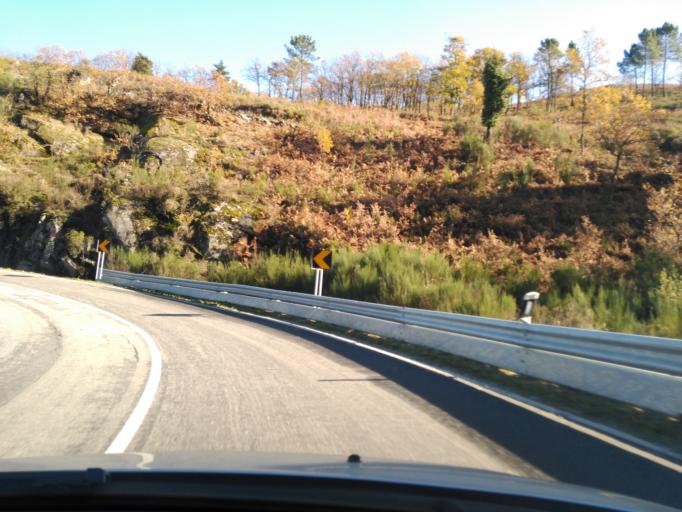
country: PT
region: Braga
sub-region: Vieira do Minho
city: Vieira do Minho
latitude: 41.6790
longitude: -8.0016
